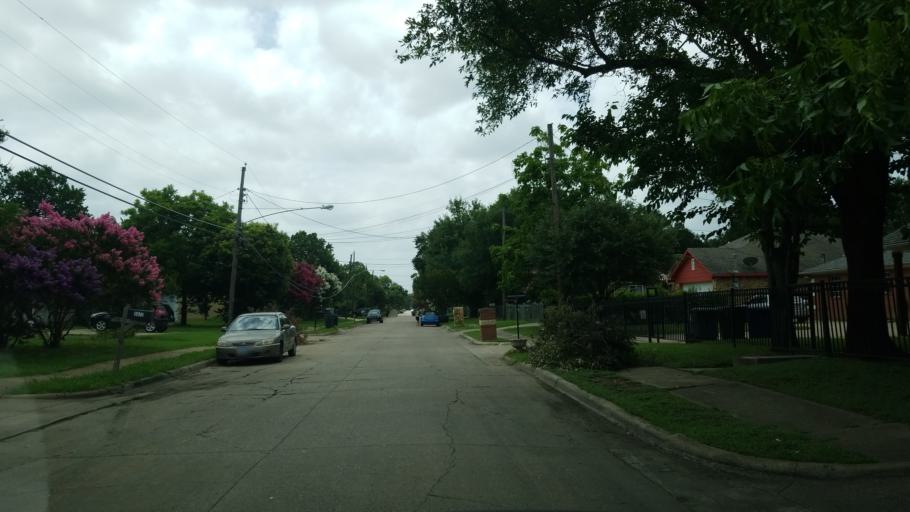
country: US
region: Texas
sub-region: Dallas County
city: Irving
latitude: 32.7870
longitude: -96.9046
